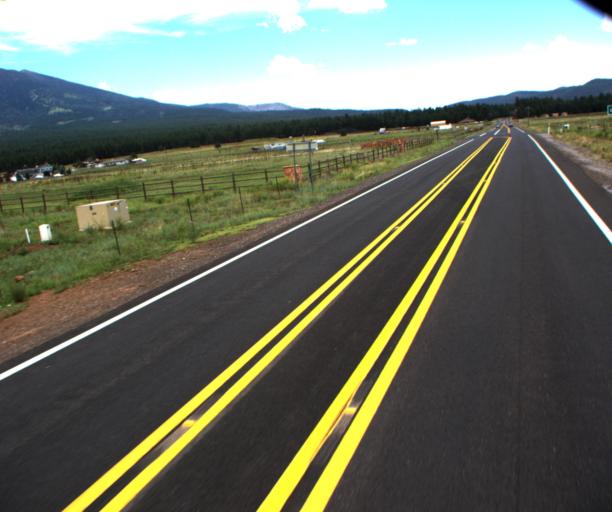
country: US
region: Arizona
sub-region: Coconino County
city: Flagstaff
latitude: 35.2681
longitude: -111.7295
